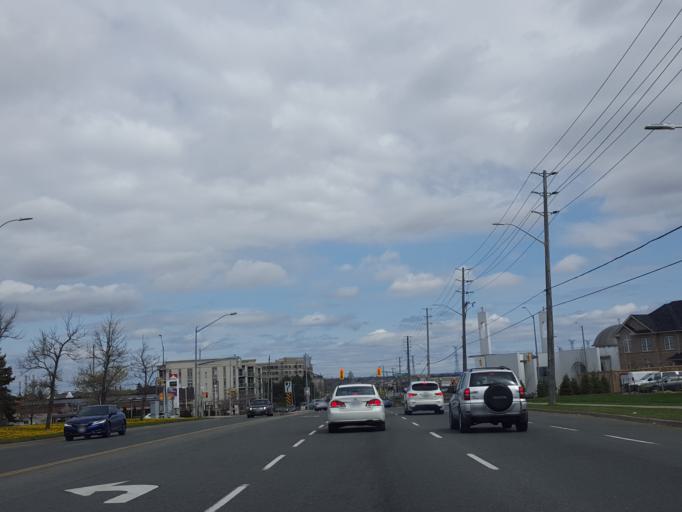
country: CA
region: Ontario
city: Markham
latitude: 43.8434
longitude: -79.2526
